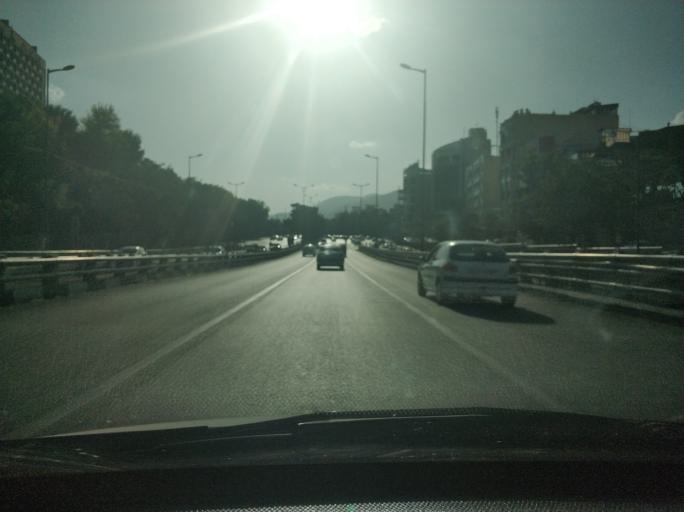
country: IR
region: Tehran
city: Tajrish
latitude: 35.7912
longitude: 51.4150
